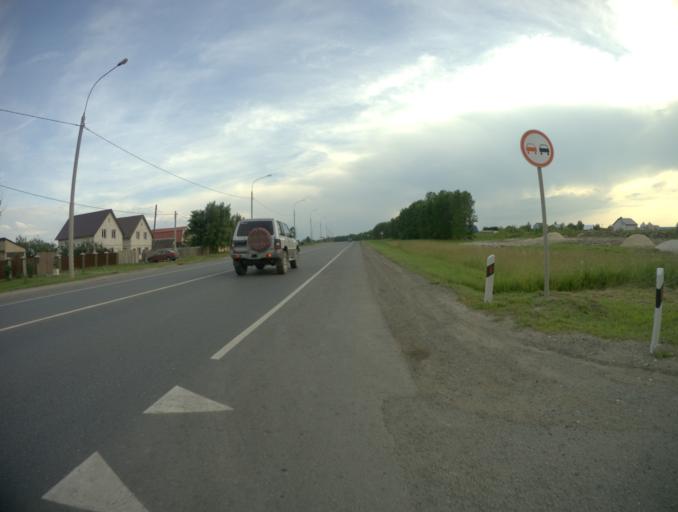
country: RU
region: Vladimir
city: Suzdal'
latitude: 56.3143
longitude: 40.4719
